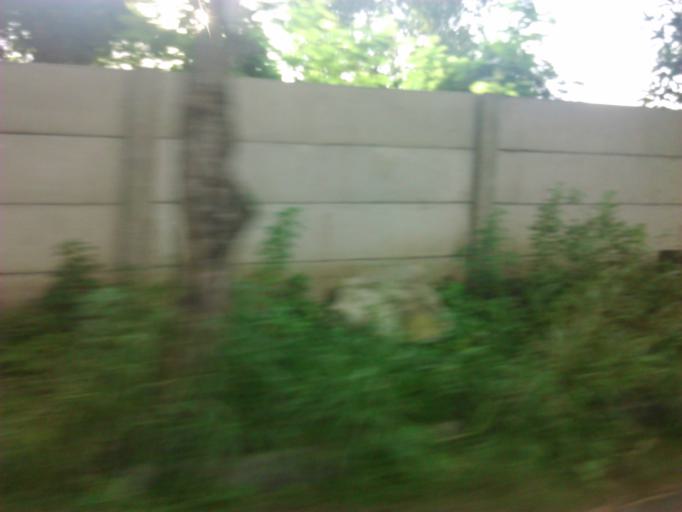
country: ID
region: East Java
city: Wonorejo
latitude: -7.2913
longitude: 112.8035
